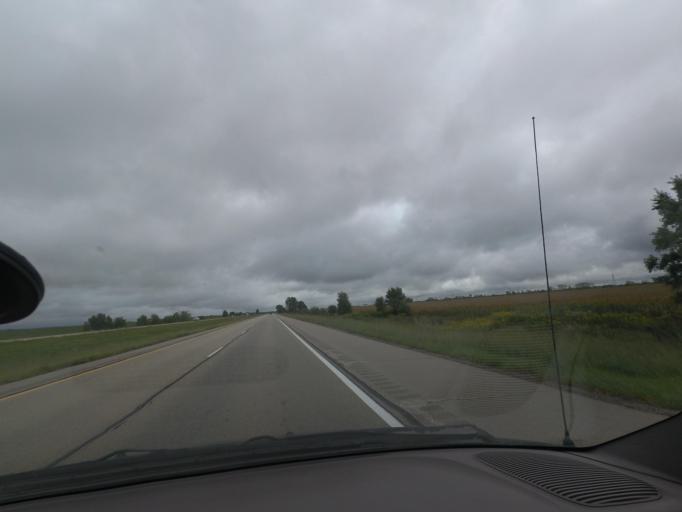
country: US
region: Illinois
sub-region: Piatt County
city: Monticello
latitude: 40.0283
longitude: -88.6575
